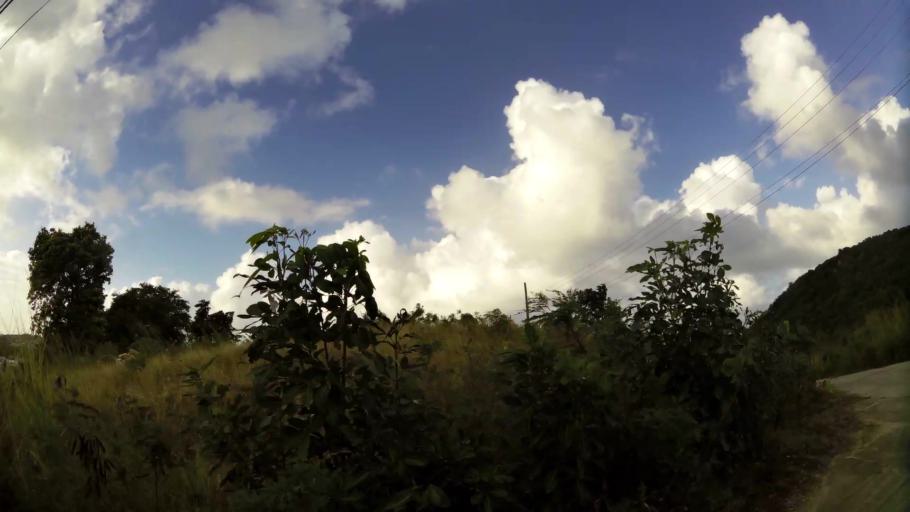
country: AG
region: Saint John
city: Saint John's
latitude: 17.1531
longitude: -61.8225
